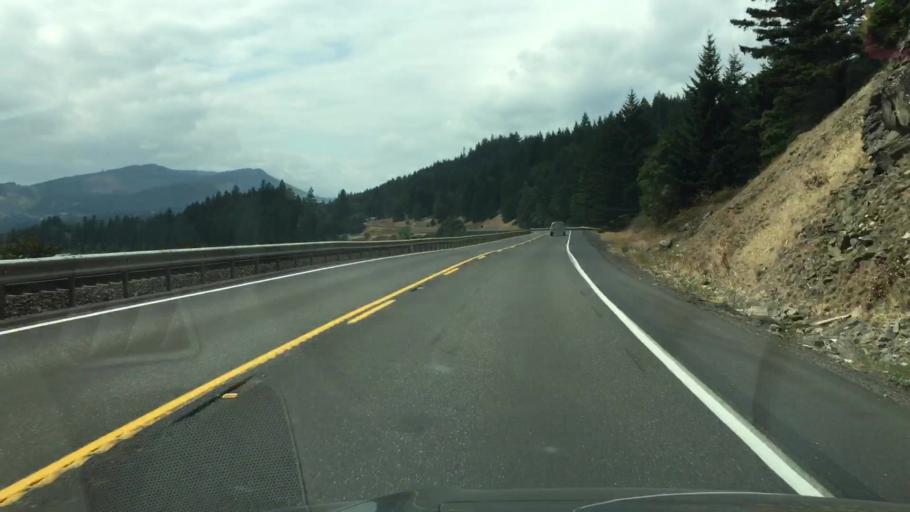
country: US
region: Washington
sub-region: Skamania County
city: Carson
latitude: 45.7051
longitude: -121.7624
